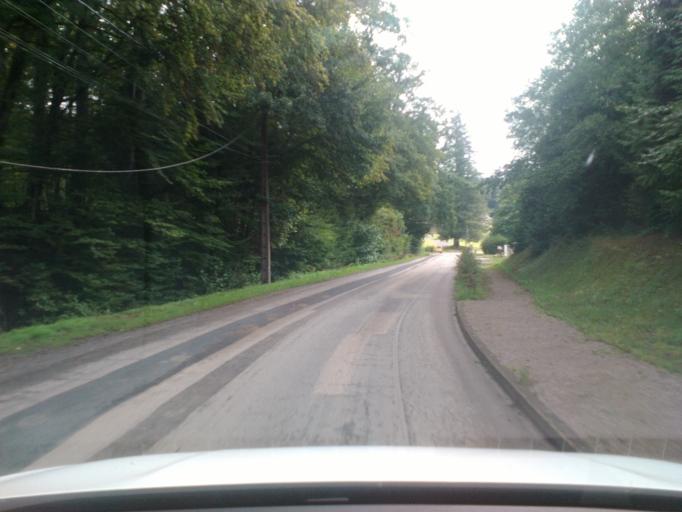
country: FR
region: Lorraine
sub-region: Departement des Vosges
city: Moyenmoutier
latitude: 48.3521
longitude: 6.9373
